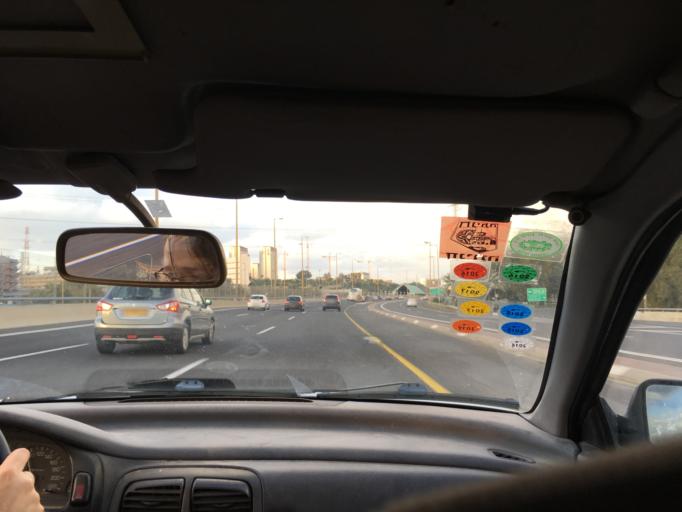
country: IL
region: Tel Aviv
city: Ramat Gan
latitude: 32.0995
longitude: 34.8029
